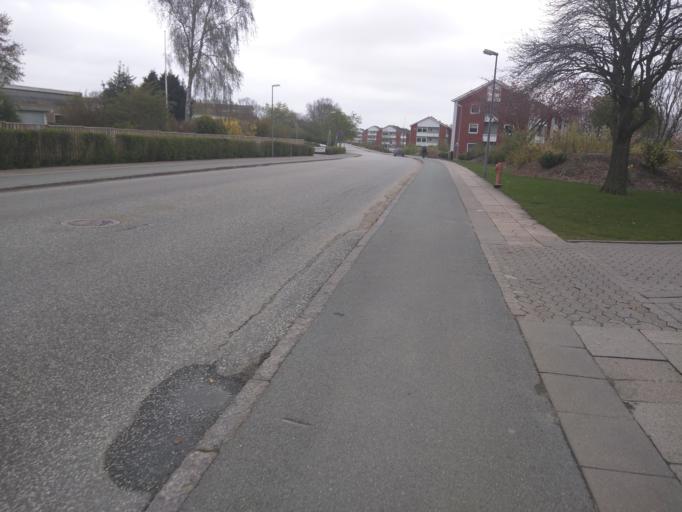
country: DK
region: Central Jutland
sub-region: Viborg Kommune
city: Viborg
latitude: 56.4620
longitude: 9.4076
